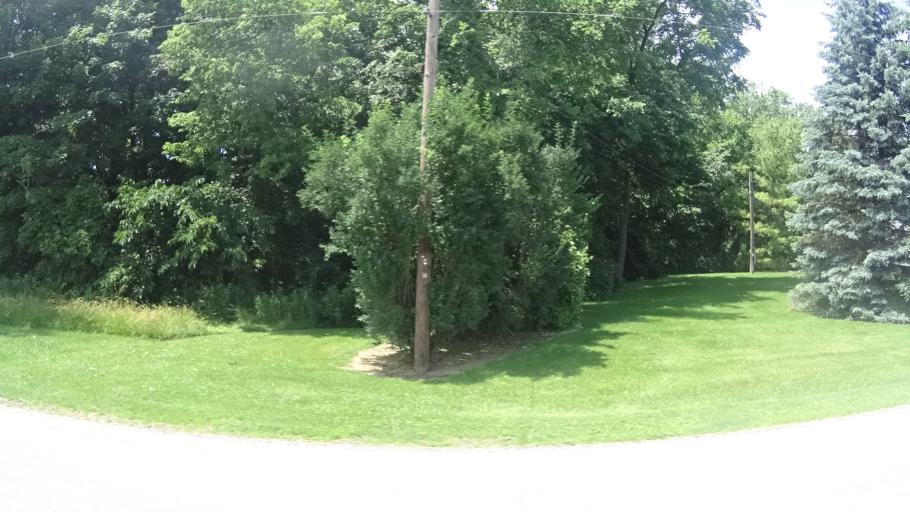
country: US
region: Ohio
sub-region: Erie County
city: Milan
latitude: 41.3273
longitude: -82.5781
